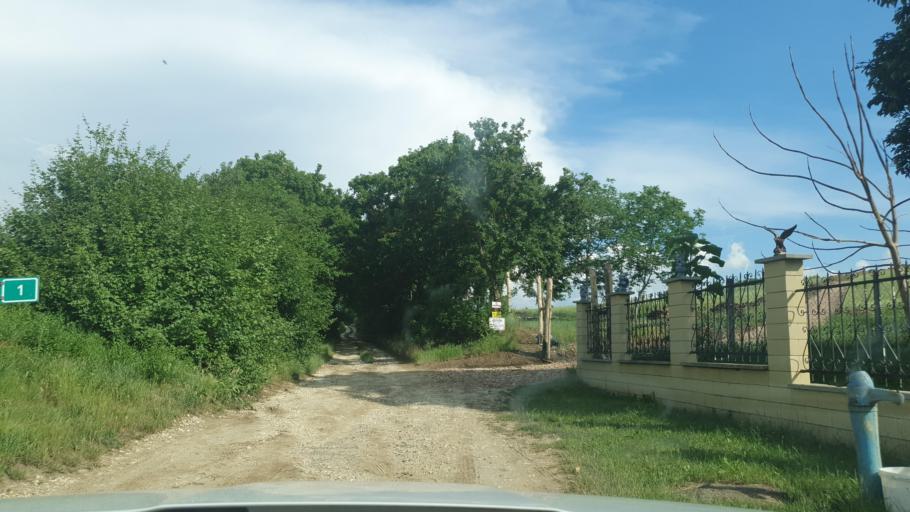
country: HU
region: Pest
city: Kosd
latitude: 47.7892
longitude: 19.2312
